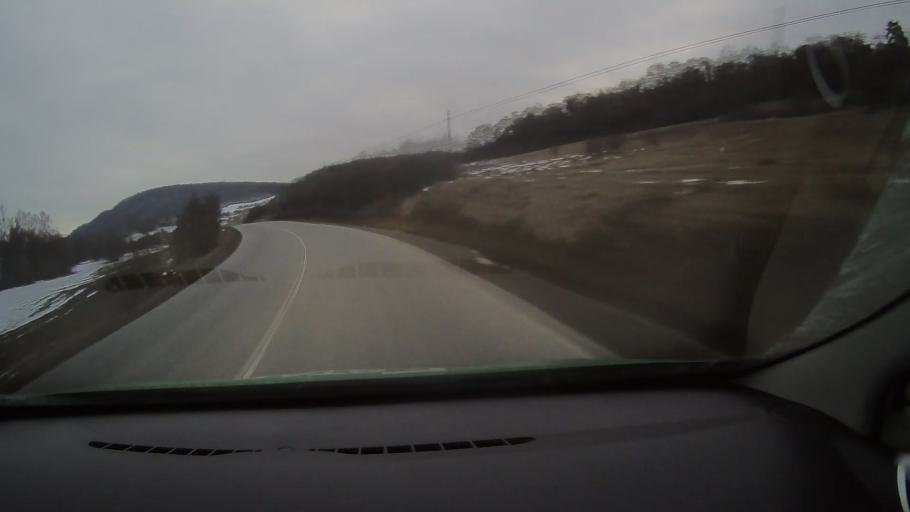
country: RO
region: Harghita
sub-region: Comuna Mugeni
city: Mugeni
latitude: 46.2326
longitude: 25.2426
